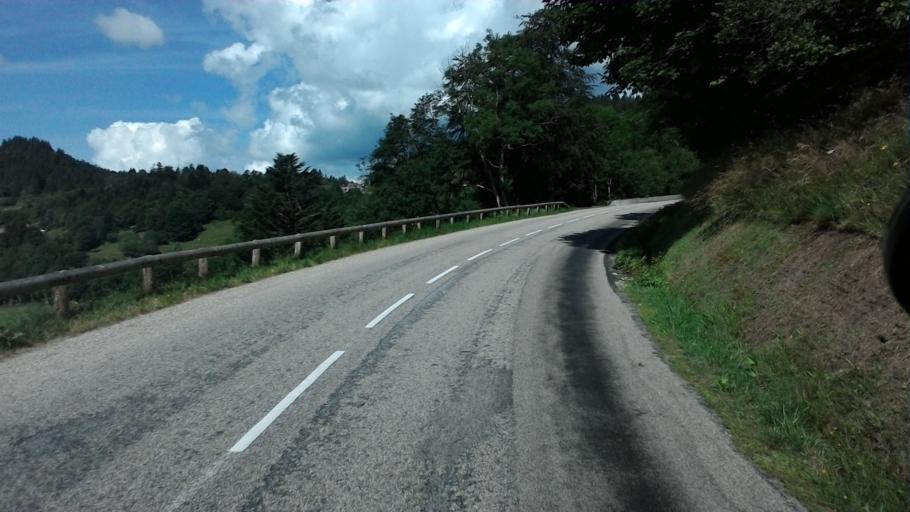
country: FR
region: Lorraine
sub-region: Departement des Vosges
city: La Bresse
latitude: 48.0249
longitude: 6.8977
